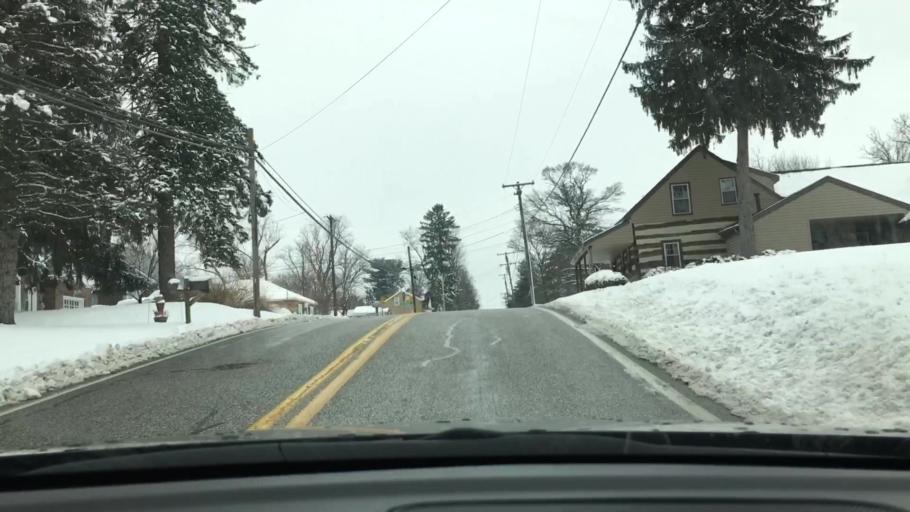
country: US
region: Pennsylvania
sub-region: York County
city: Emigsville
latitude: 40.0081
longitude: -76.7534
